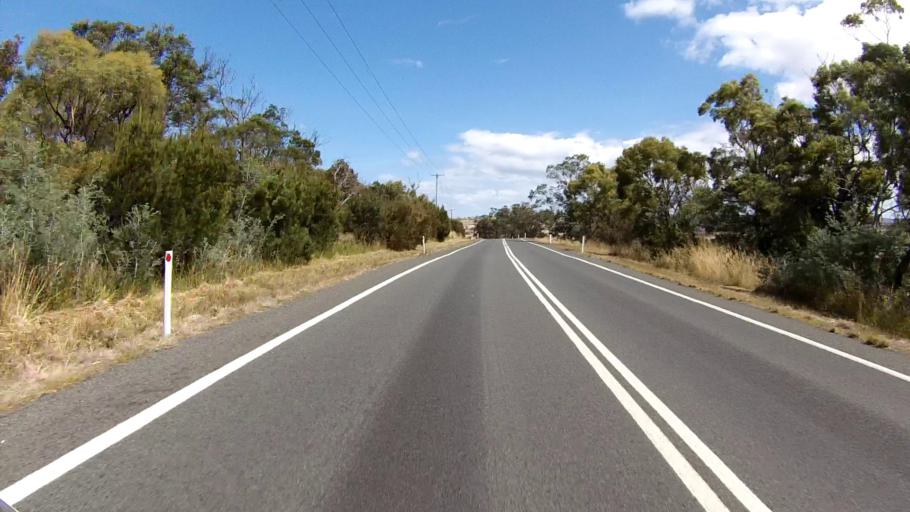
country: AU
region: Tasmania
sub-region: Break O'Day
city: St Helens
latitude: -42.0827
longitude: 148.0681
